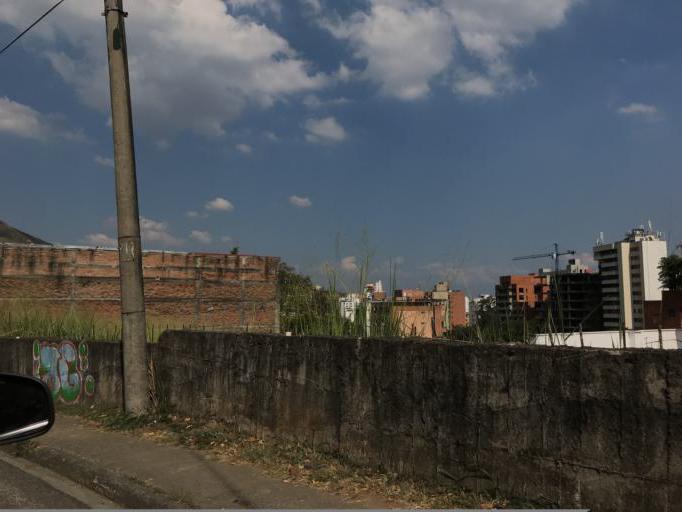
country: CO
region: Valle del Cauca
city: Cali
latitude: 3.4511
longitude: -76.5549
